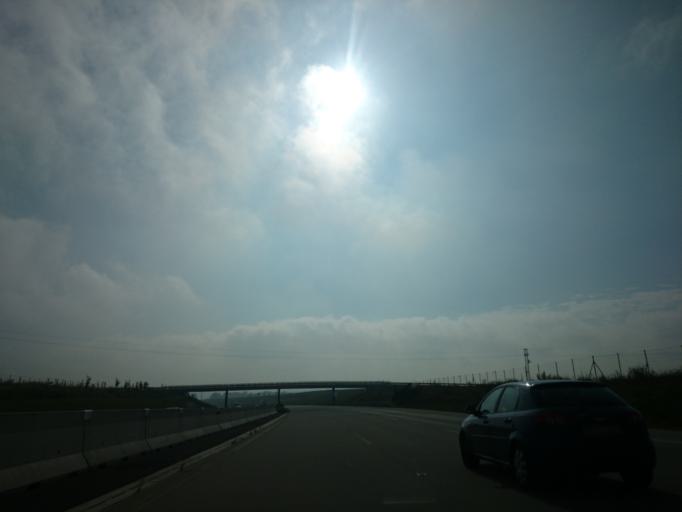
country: CZ
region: Olomoucky
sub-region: Okres Prerov
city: Hranice
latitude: 49.5726
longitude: 17.6835
